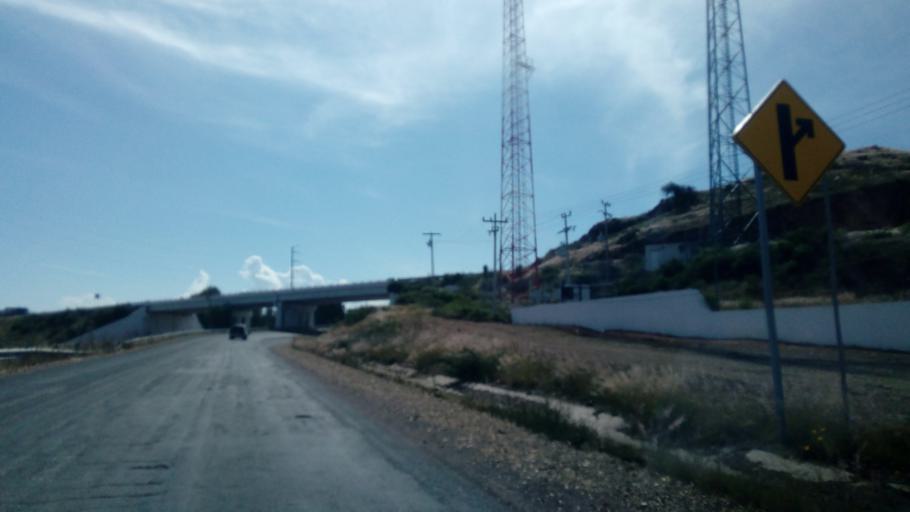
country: MX
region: Durango
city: Victoria de Durango
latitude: 24.0705
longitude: -104.6555
